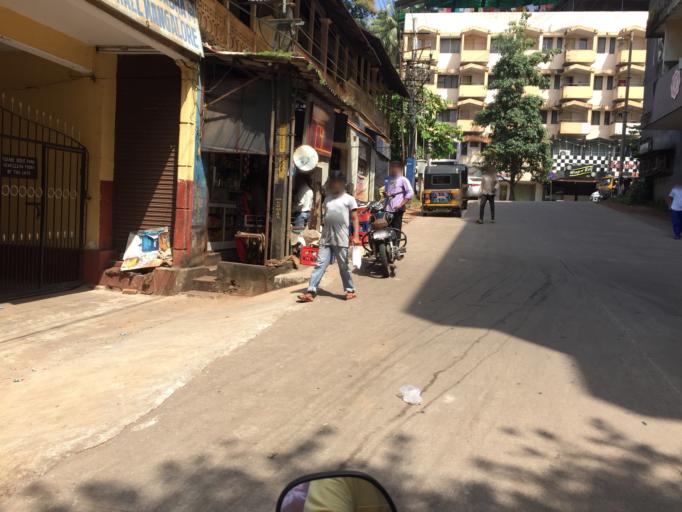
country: IN
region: Karnataka
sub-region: Dakshina Kannada
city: Mangalore
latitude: 12.8708
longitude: 74.8473
